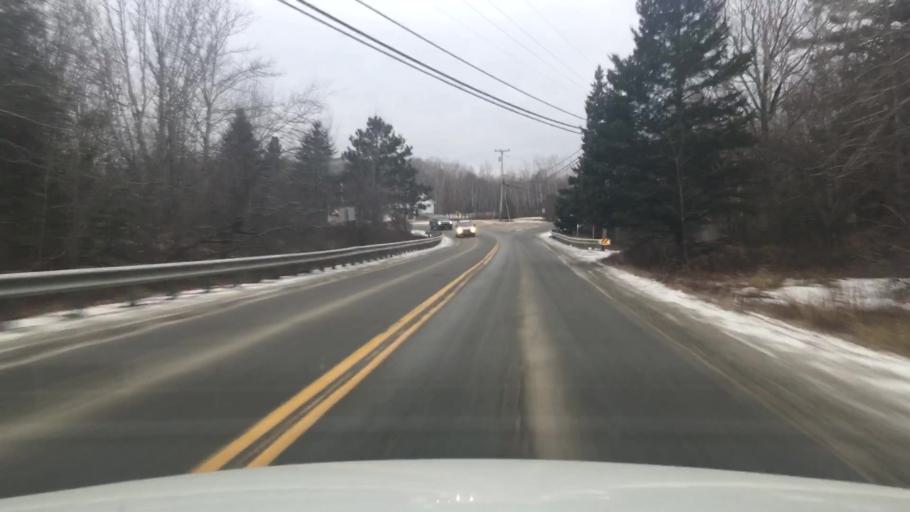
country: US
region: Maine
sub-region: Hancock County
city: Trenton
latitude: 44.5001
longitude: -68.3585
